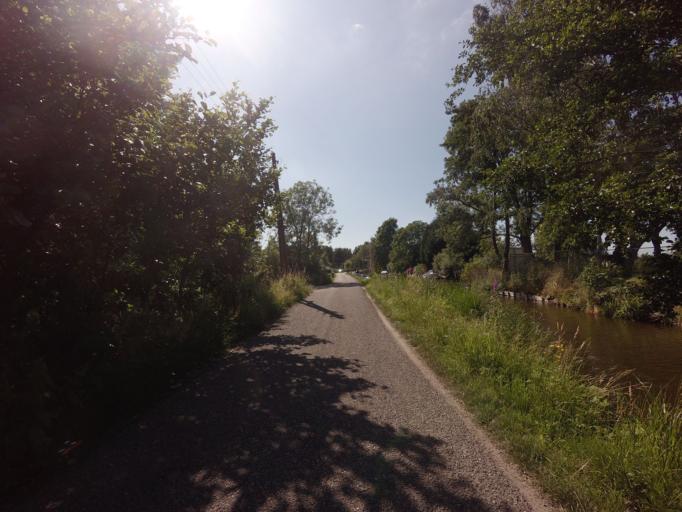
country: NL
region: South Holland
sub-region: Bodegraven-Reeuwijk
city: Reeuwijk
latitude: 52.0237
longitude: 4.7407
